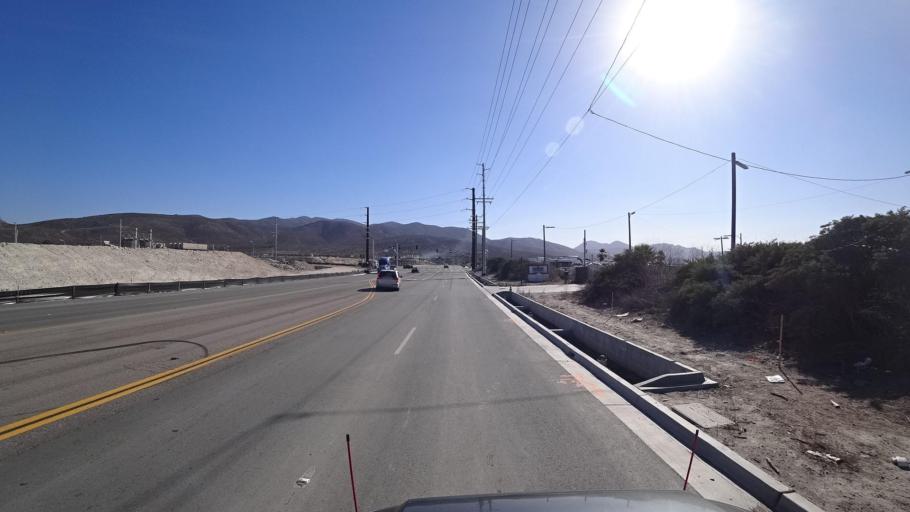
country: MX
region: Baja California
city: Tijuana
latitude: 32.5673
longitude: -116.9207
